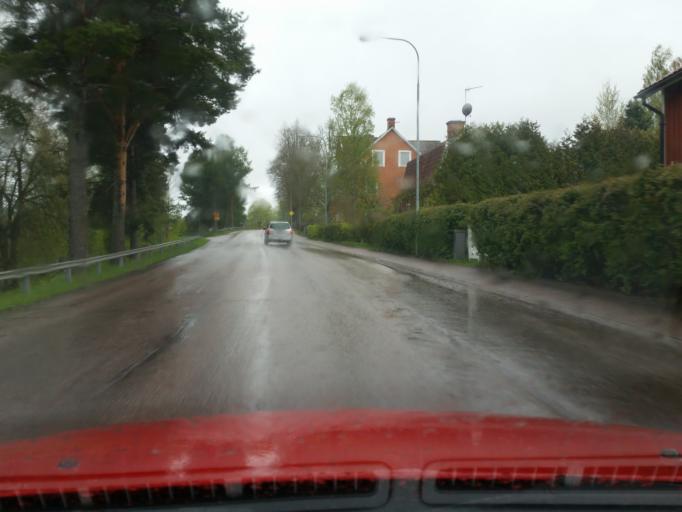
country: SE
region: Dalarna
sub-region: Hedemora Kommun
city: Hedemora
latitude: 60.2854
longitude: 15.9760
